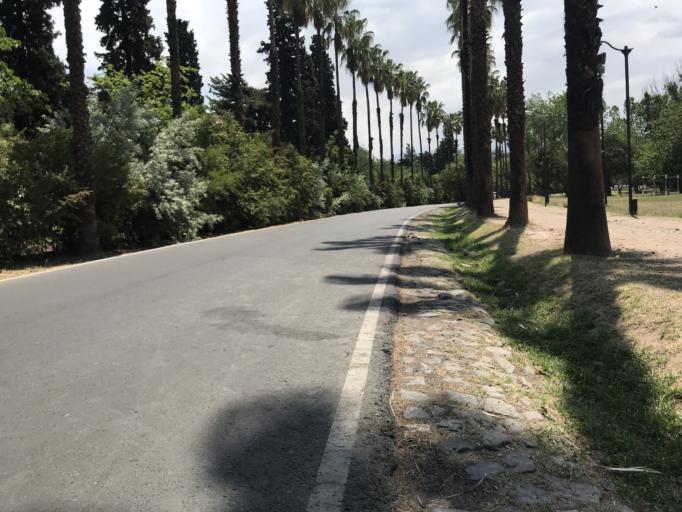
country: AR
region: Mendoza
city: Mendoza
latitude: -32.8942
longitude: -68.8695
